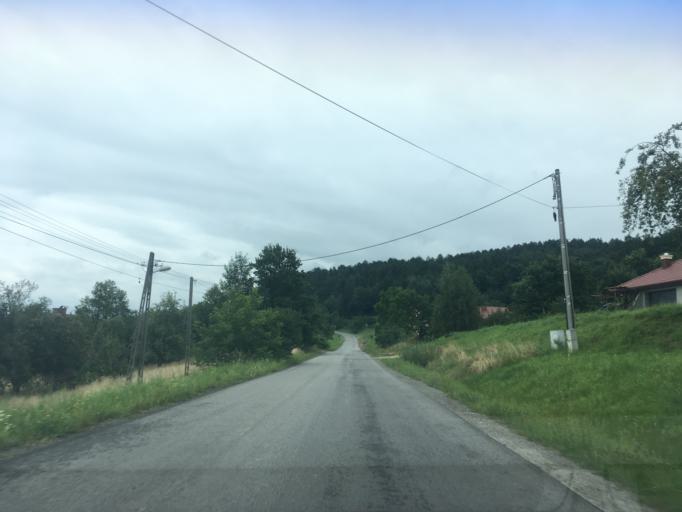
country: PL
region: Lesser Poland Voivodeship
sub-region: Powiat myslenicki
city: Brzaczowice
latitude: 49.8551
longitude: 20.0284
